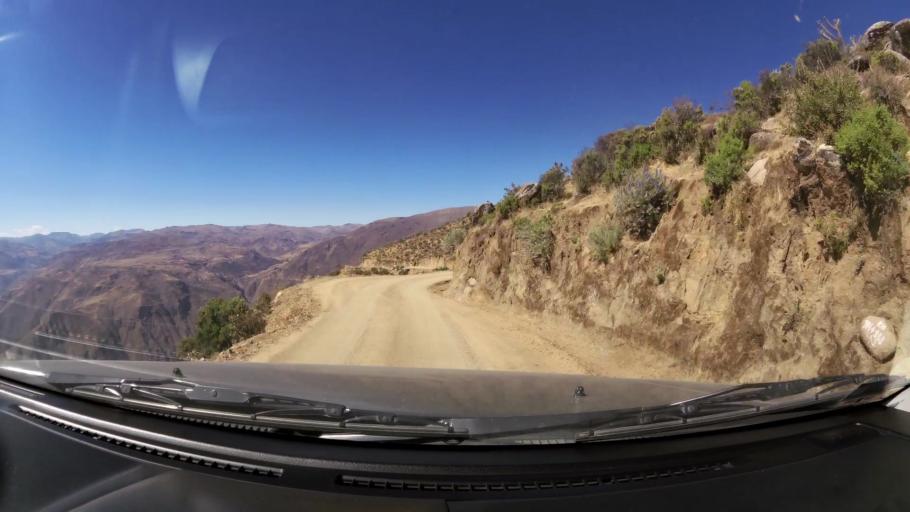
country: PE
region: Huancavelica
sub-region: Huaytara
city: Quito-Arma
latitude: -13.6249
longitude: -75.3541
